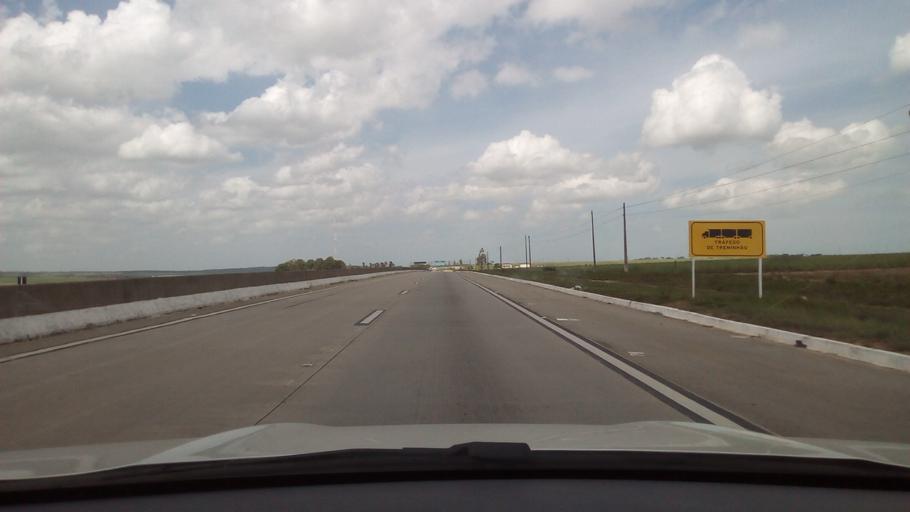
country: BR
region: Paraiba
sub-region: Mamanguape
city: Mamanguape
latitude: -6.8012
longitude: -35.1392
